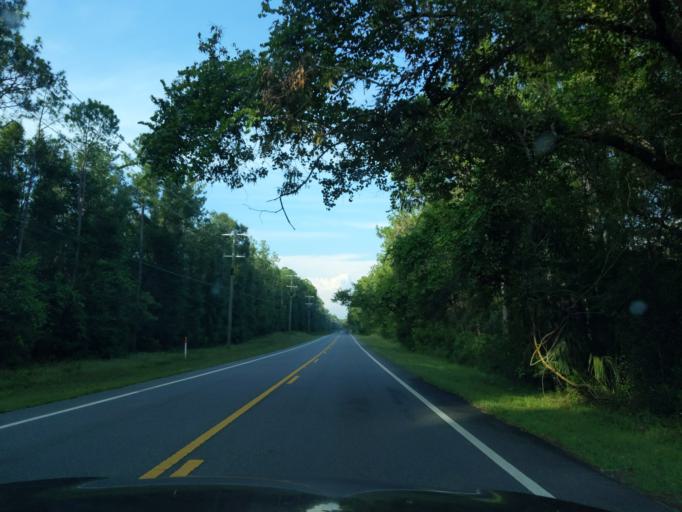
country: US
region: Florida
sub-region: Leon County
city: Tallahassee
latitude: 30.3821
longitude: -84.3431
